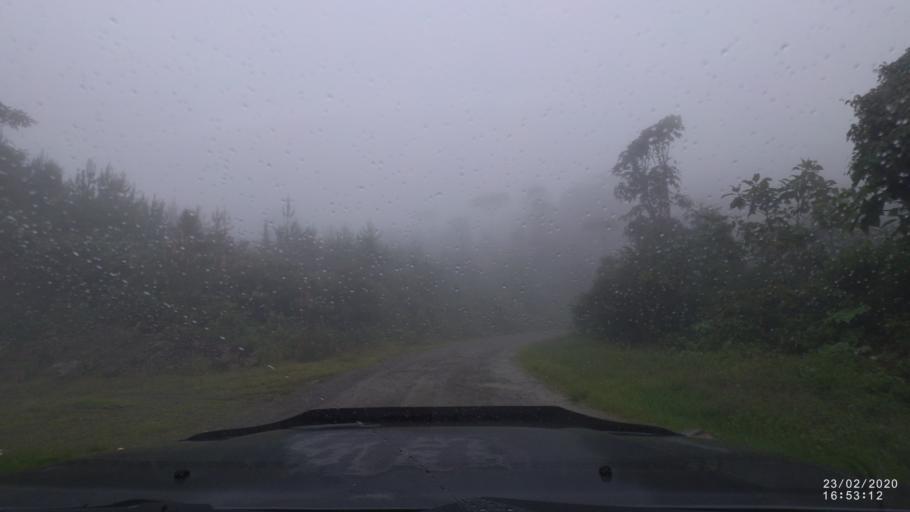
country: BO
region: Cochabamba
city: Colomi
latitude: -17.0961
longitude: -65.9830
